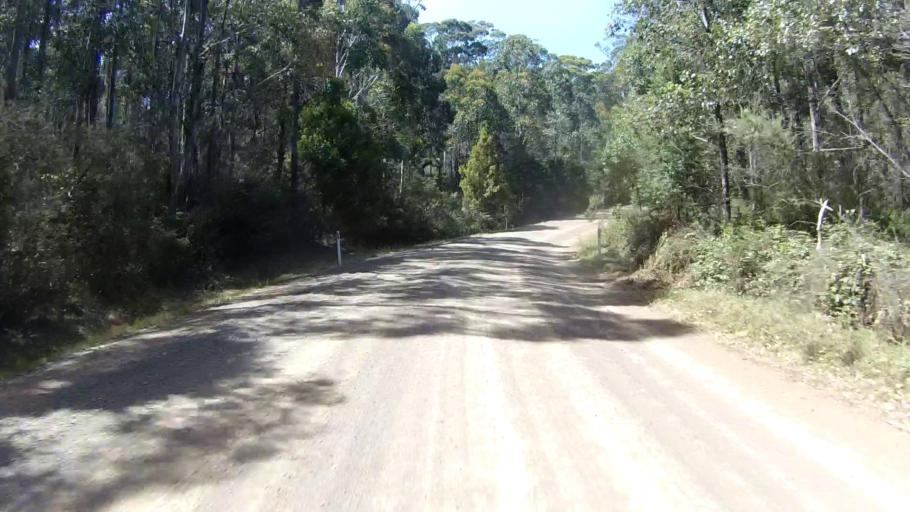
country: AU
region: Tasmania
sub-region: Sorell
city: Sorell
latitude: -42.7003
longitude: 147.7436
